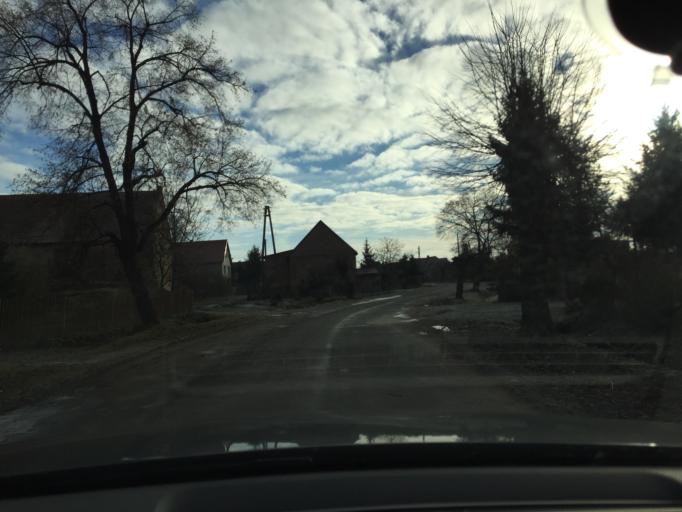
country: PL
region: Lower Silesian Voivodeship
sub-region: Powiat sredzki
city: Udanin
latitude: 51.0555
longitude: 16.4920
